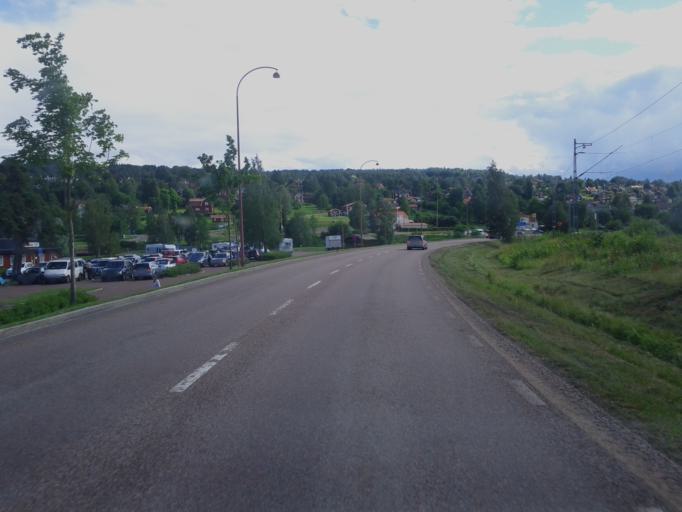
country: SE
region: Dalarna
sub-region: Rattviks Kommun
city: Raettvik
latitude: 60.8827
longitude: 15.1183
